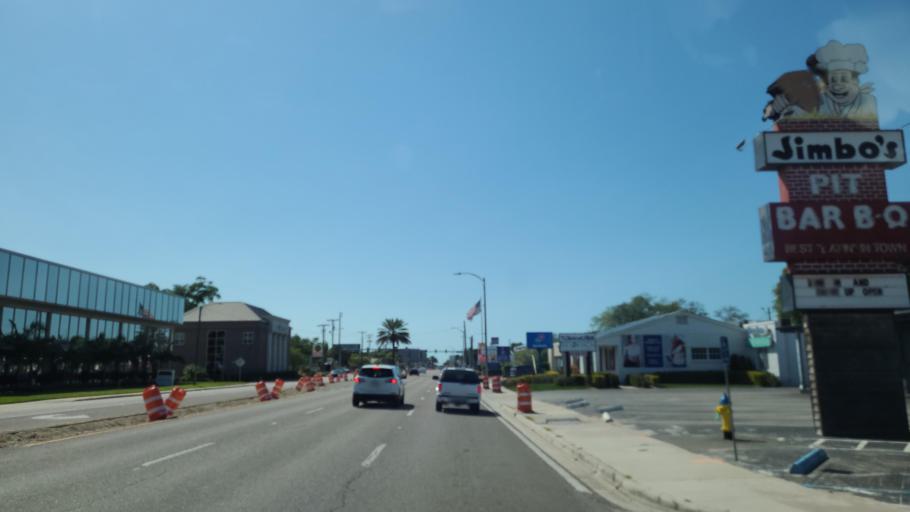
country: US
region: Florida
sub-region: Hillsborough County
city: Tampa
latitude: 27.9452
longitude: -82.5106
